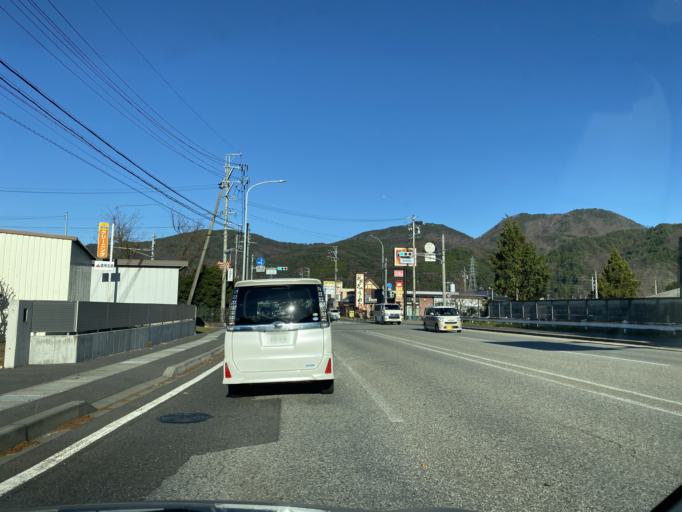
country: JP
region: Nagano
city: Omachi
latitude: 36.4930
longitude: 137.8598
